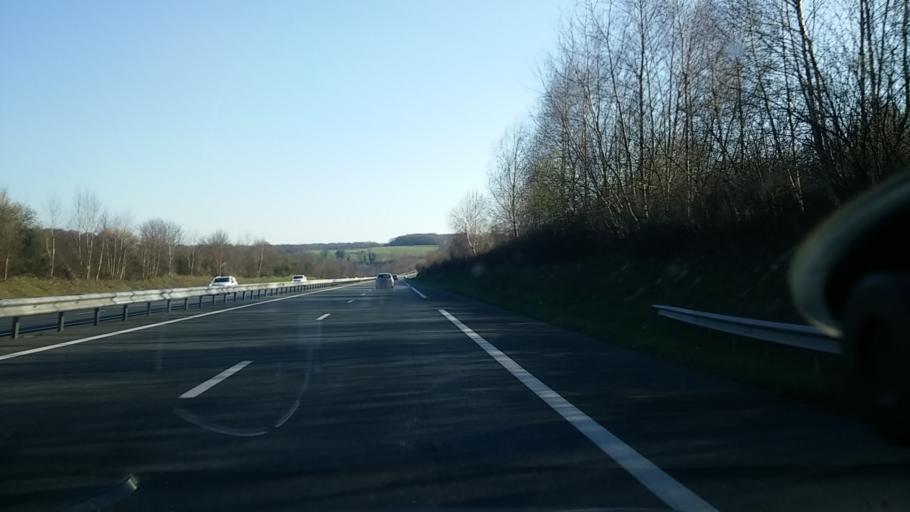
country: FR
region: Limousin
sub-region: Departement de la Haute-Vienne
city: Saint-Sulpice-les-Feuilles
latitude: 46.3867
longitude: 1.4490
